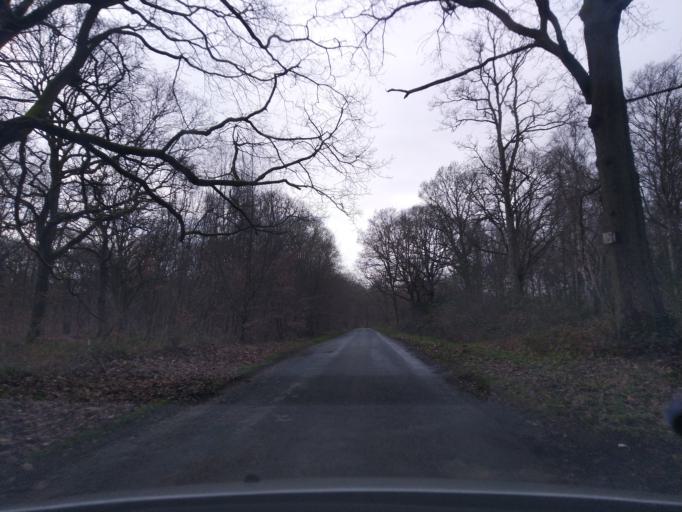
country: FR
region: Haute-Normandie
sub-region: Departement de la Seine-Maritime
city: Saint-Pierre-de-Varengeville
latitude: 49.4942
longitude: 0.9071
